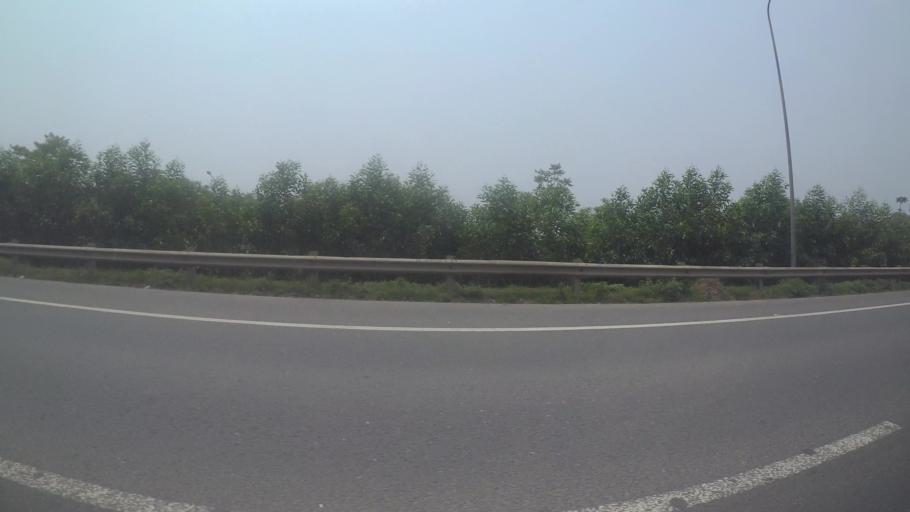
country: VN
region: Ha Noi
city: Quoc Oai
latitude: 20.9889
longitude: 105.5743
